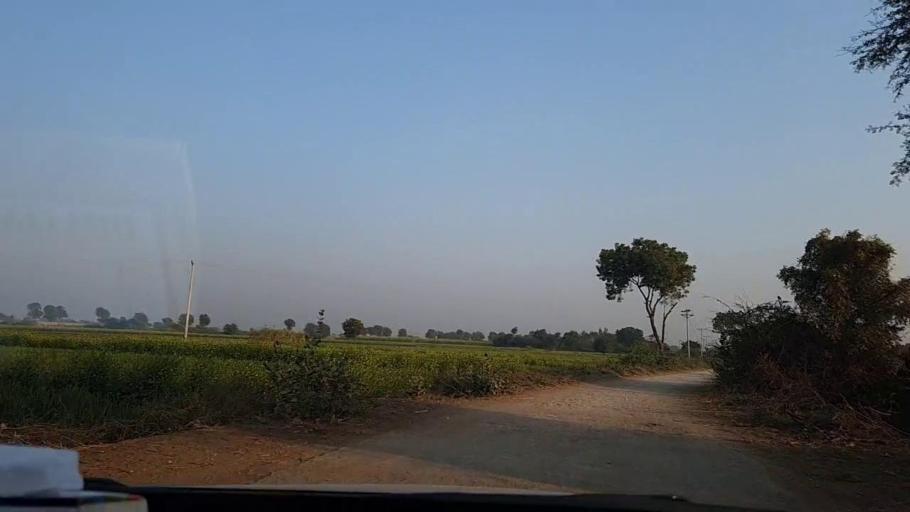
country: PK
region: Sindh
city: Tando Ghulam Ali
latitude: 25.1857
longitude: 68.9194
